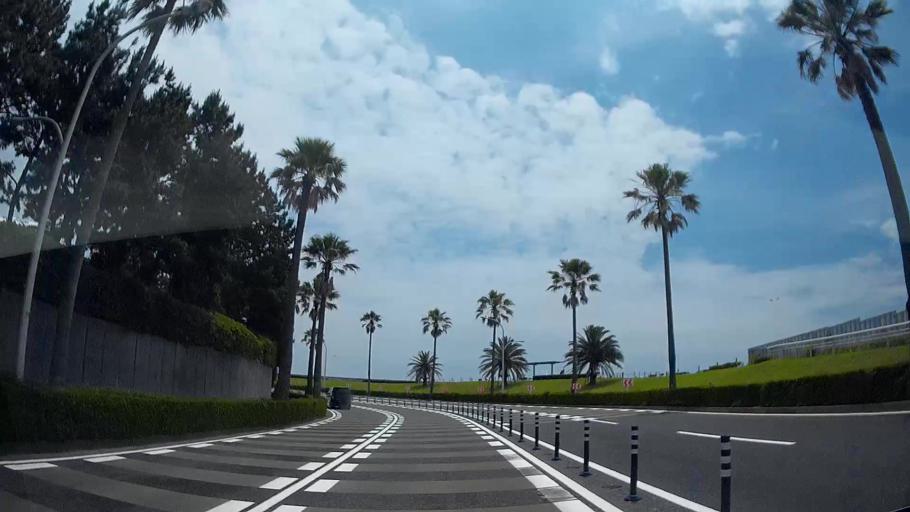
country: JP
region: Tokyo
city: Urayasu
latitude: 35.6266
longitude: 139.8731
